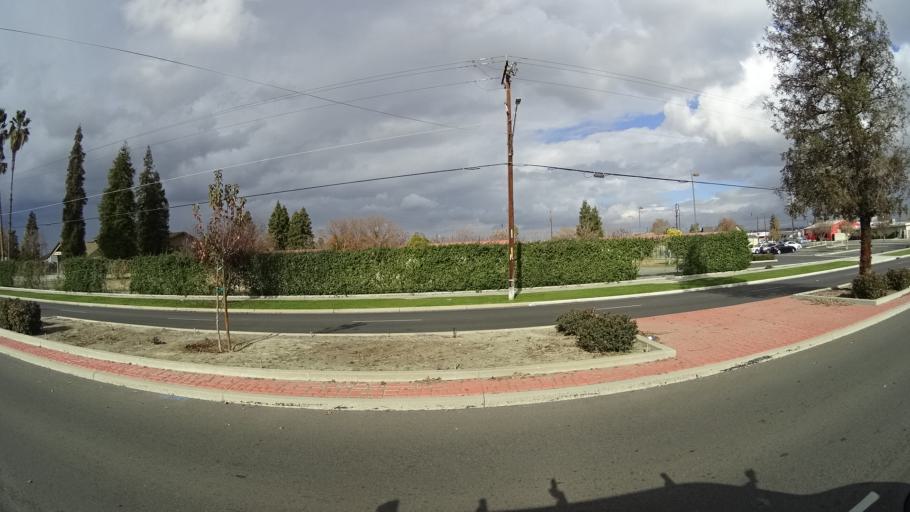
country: US
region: California
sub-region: Kern County
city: Bakersfield
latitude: 35.3732
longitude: -118.9984
